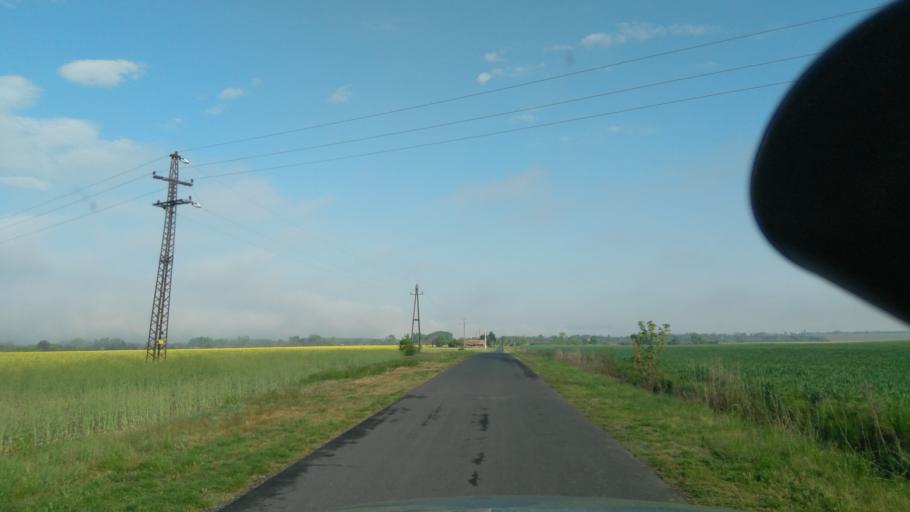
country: HU
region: Zala
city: Sarmellek
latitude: 46.7337
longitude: 17.1506
